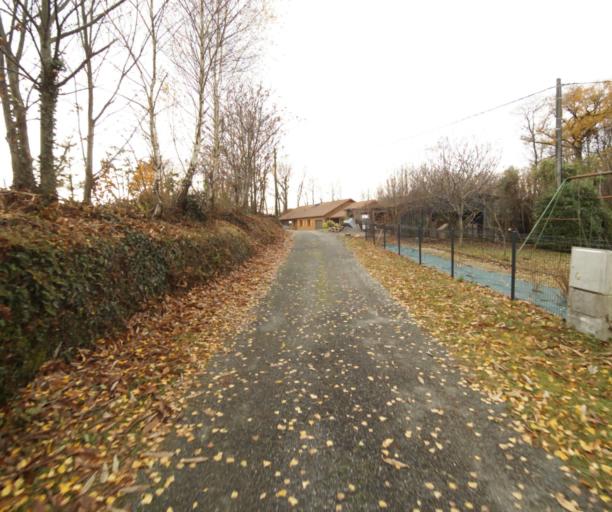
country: FR
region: Limousin
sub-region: Departement de la Correze
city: Sainte-Fortunade
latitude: 45.1770
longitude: 1.7543
